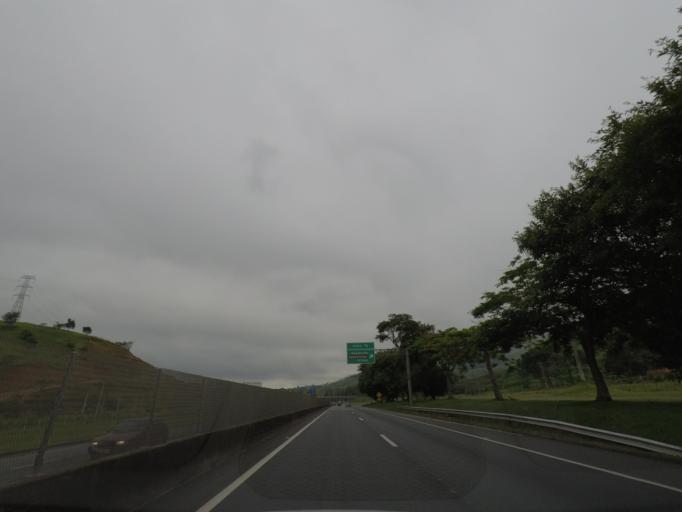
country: BR
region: Sao Paulo
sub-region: Aparecida
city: Aparecida
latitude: -22.8751
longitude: -45.2623
